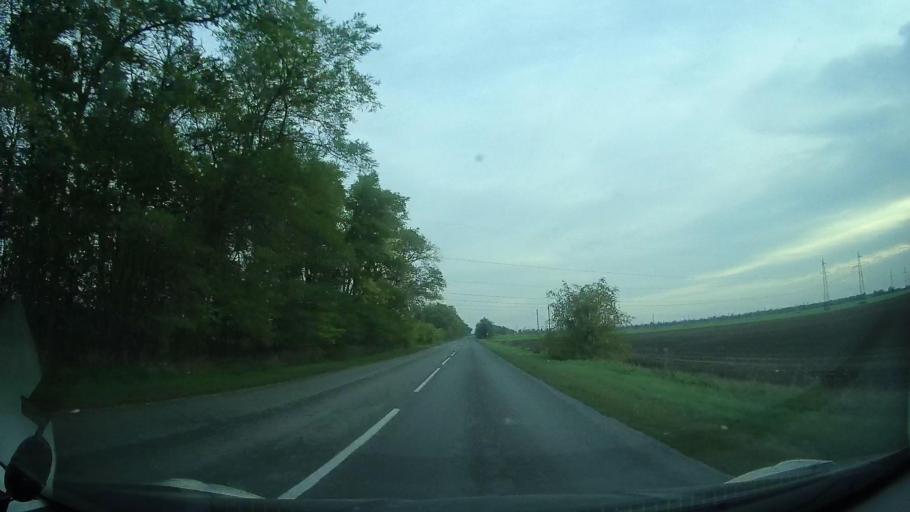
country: RU
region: Rostov
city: Ol'ginskaya
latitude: 47.1120
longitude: 39.9773
